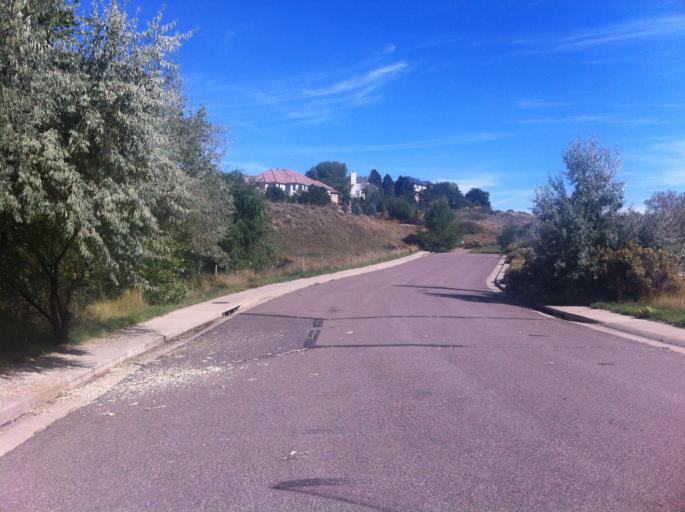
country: US
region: Colorado
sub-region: Jefferson County
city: Lakewood
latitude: 39.6747
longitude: -105.1285
